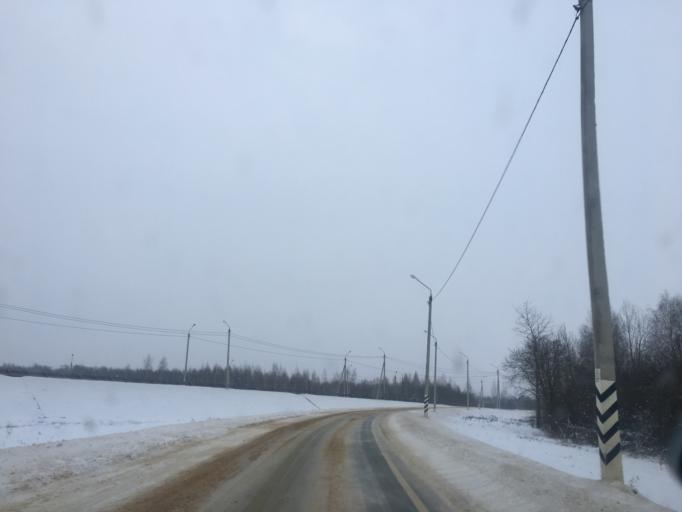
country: RU
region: Tula
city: Kosaya Gora
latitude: 54.1575
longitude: 37.4941
